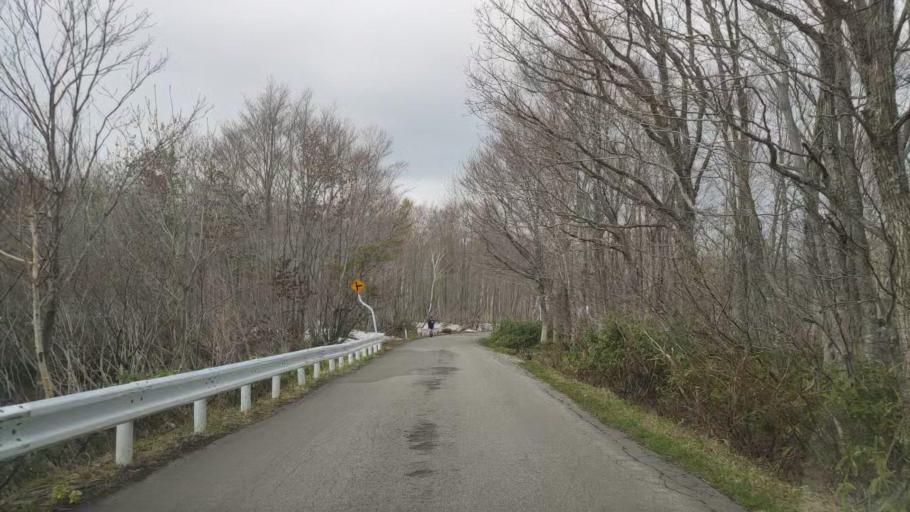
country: JP
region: Aomori
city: Aomori Shi
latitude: 40.6952
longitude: 140.9095
